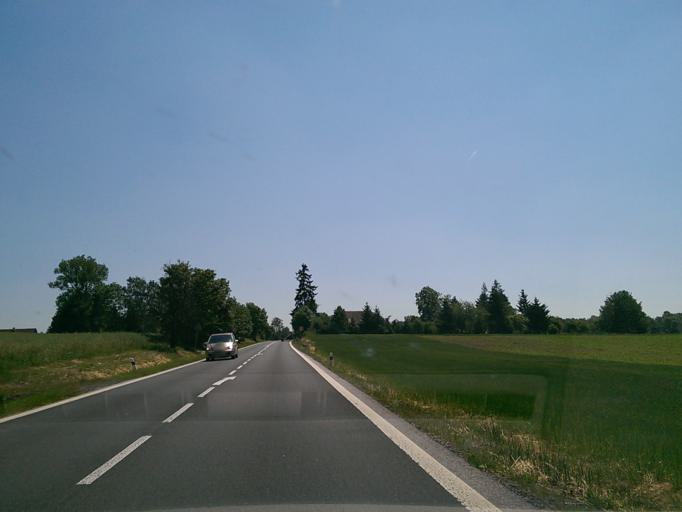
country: CZ
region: Liberecky
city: Rovensko pod Troskami
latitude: 50.5051
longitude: 15.2814
